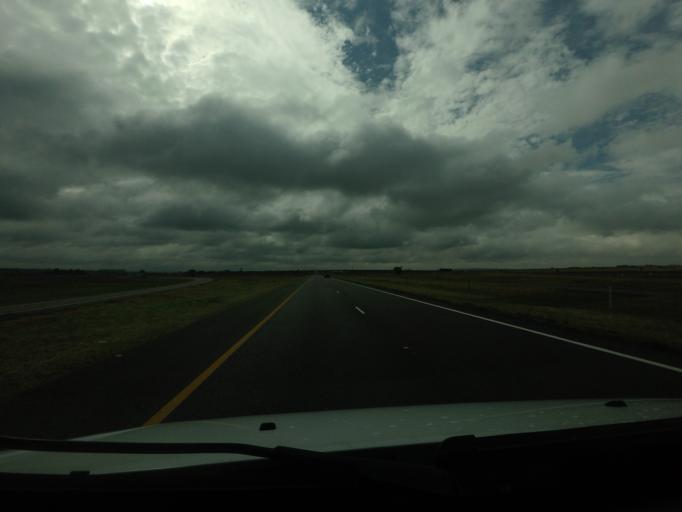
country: ZA
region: Gauteng
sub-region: City of Tshwane Metropolitan Municipality
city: Bronkhorstspruit
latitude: -25.8064
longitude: 28.6918
